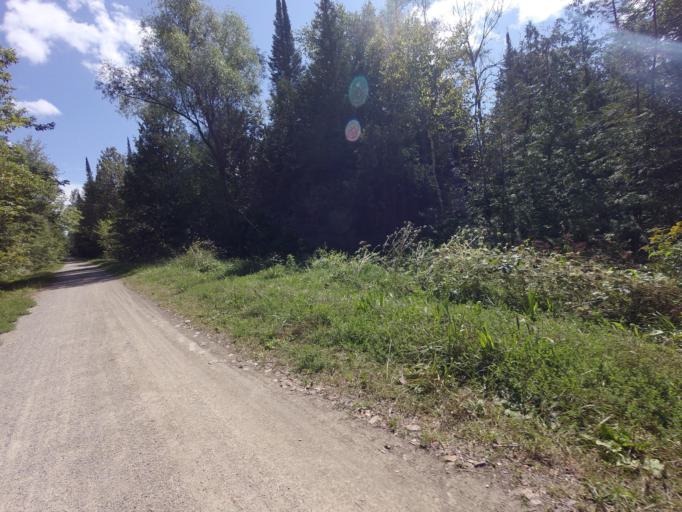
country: CA
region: Ontario
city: Orangeville
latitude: 43.7823
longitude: -80.2230
